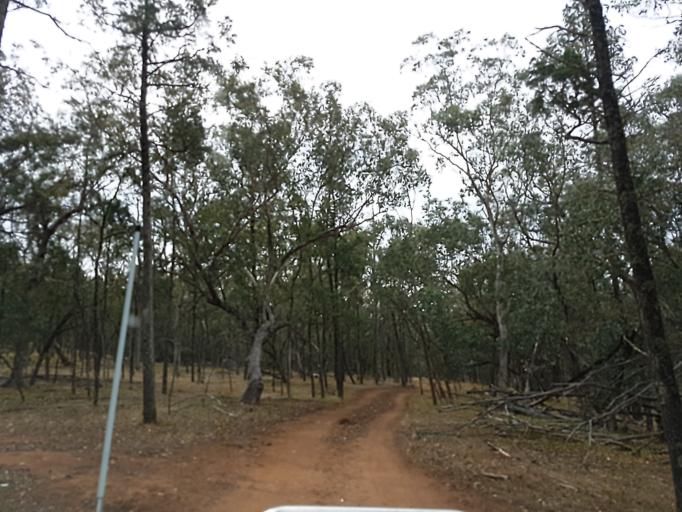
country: AU
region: New South Wales
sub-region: Snowy River
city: Jindabyne
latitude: -36.9578
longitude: 148.4094
